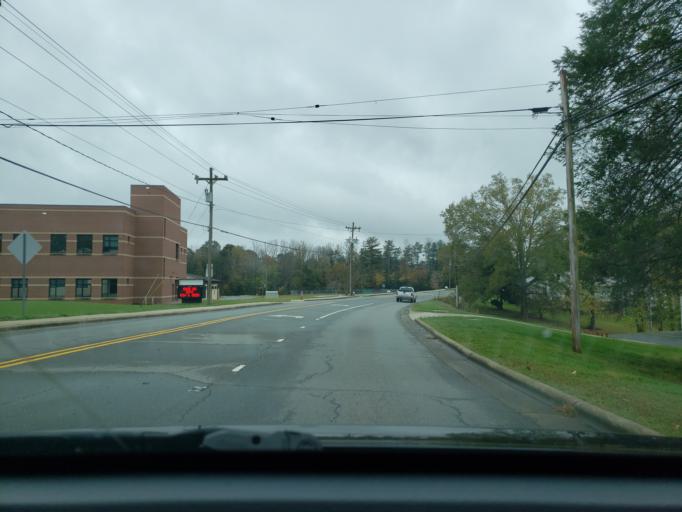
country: US
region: North Carolina
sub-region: Stokes County
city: Walnut Cove
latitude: 36.3108
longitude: -80.1396
